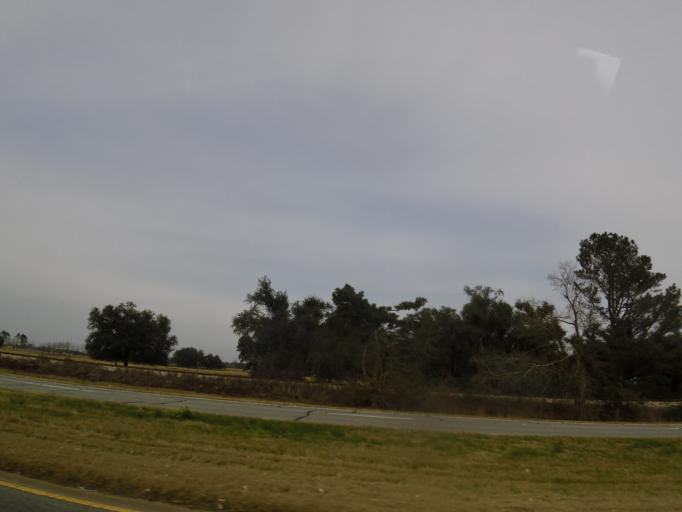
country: US
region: Georgia
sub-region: Seminole County
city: Donalsonville
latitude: 31.0333
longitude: -84.8598
